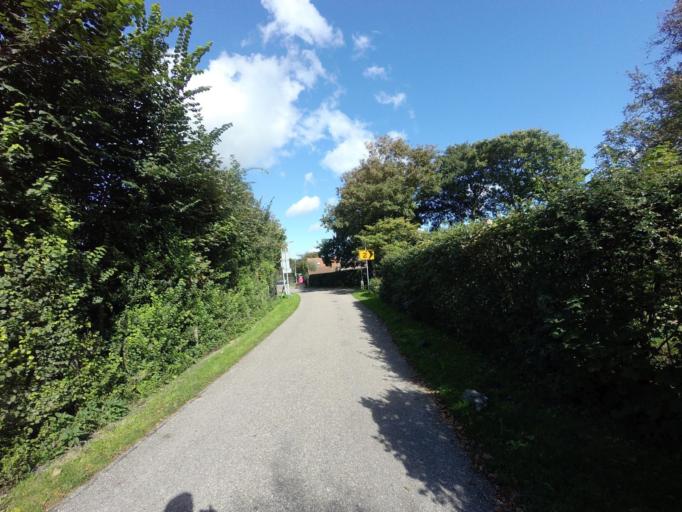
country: NL
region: North Holland
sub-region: Gemeente Bergen
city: Egmond aan Zee
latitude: 52.7216
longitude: 4.6620
